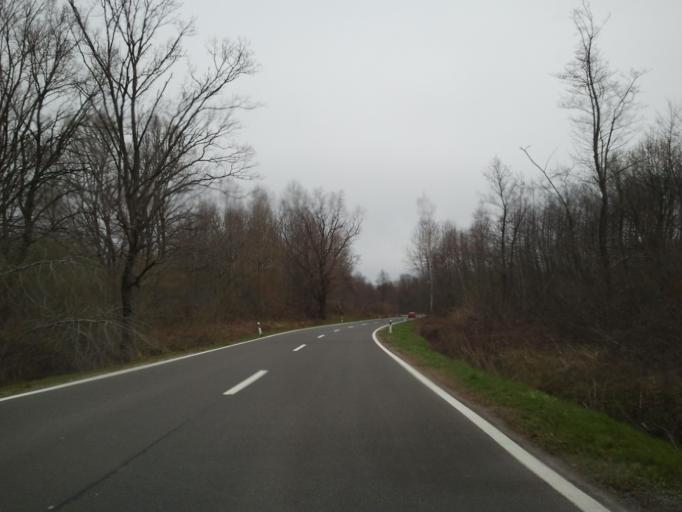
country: HR
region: Sisacko-Moslavacka
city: Gvozd
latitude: 45.3249
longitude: 15.9665
